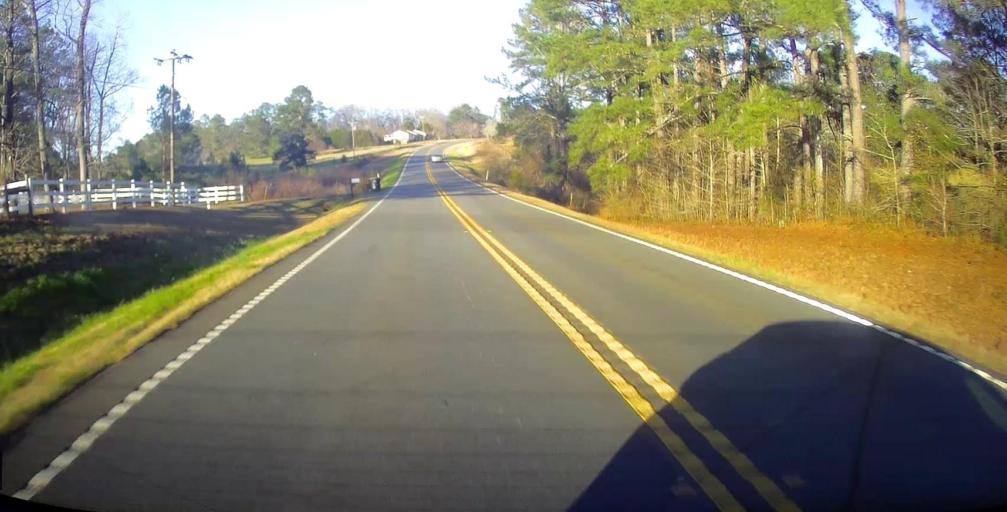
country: US
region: Georgia
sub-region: Upson County
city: Thomaston
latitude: 32.8759
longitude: -84.3898
